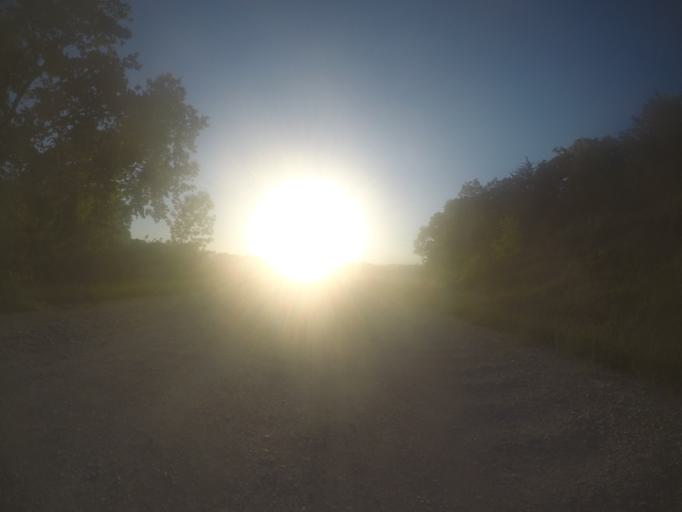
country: US
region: Kansas
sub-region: Riley County
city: Manhattan
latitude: 39.2421
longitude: -96.5618
